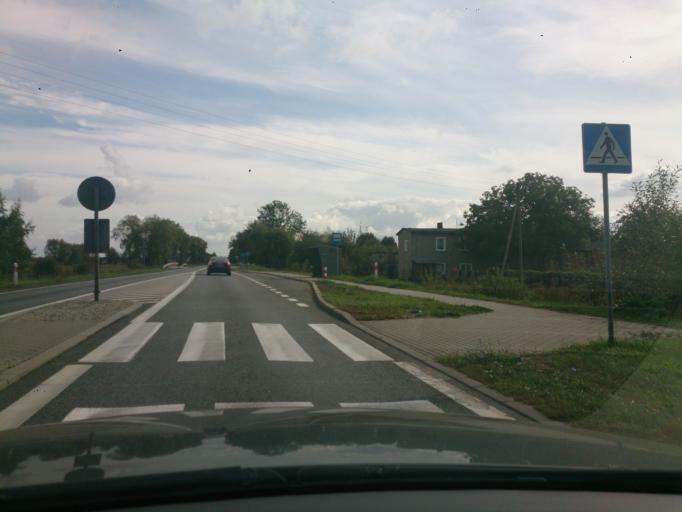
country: PL
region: Kujawsko-Pomorskie
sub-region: Grudziadz
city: Grudziadz
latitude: 53.4956
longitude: 18.6965
